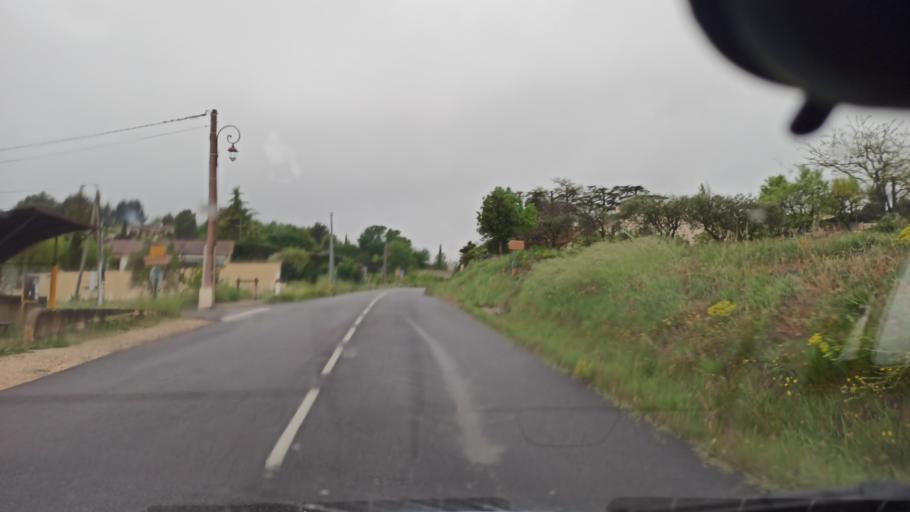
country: FR
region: Provence-Alpes-Cote d'Azur
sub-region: Departement du Vaucluse
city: Gargas
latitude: 43.8959
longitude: 5.3598
